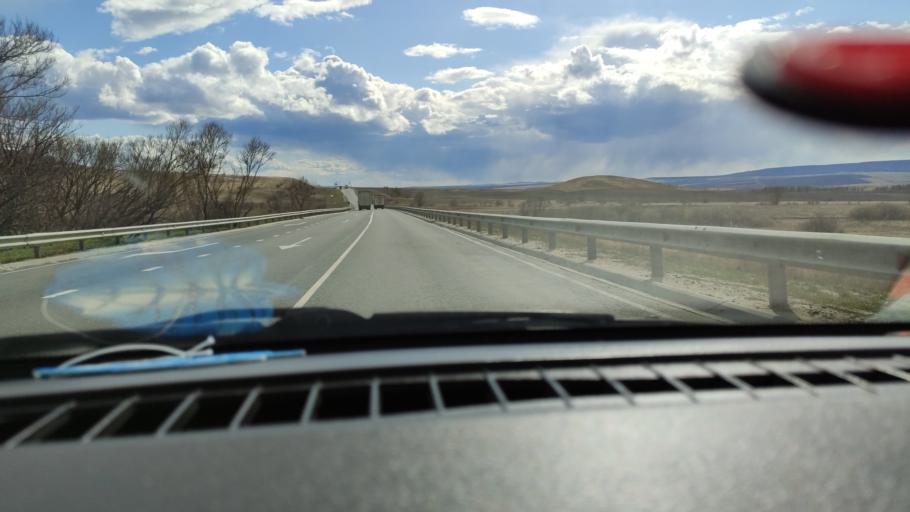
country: RU
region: Saratov
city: Alekseyevka
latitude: 52.3497
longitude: 47.9396
